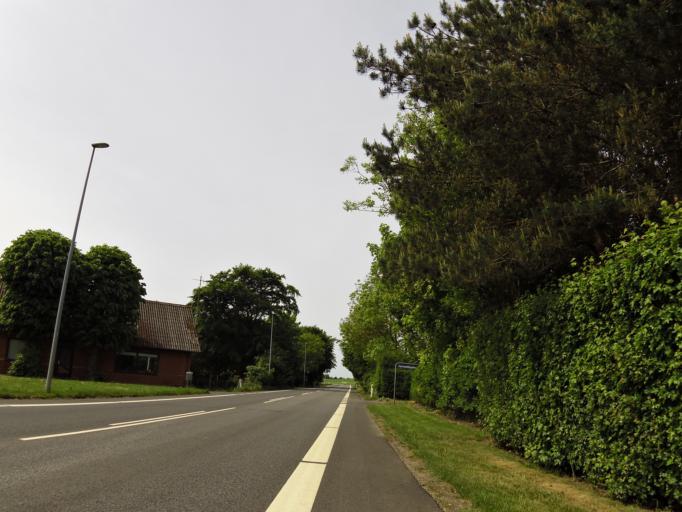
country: DK
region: Central Jutland
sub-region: Holstebro Kommune
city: Vinderup
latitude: 56.5770
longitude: 8.8504
